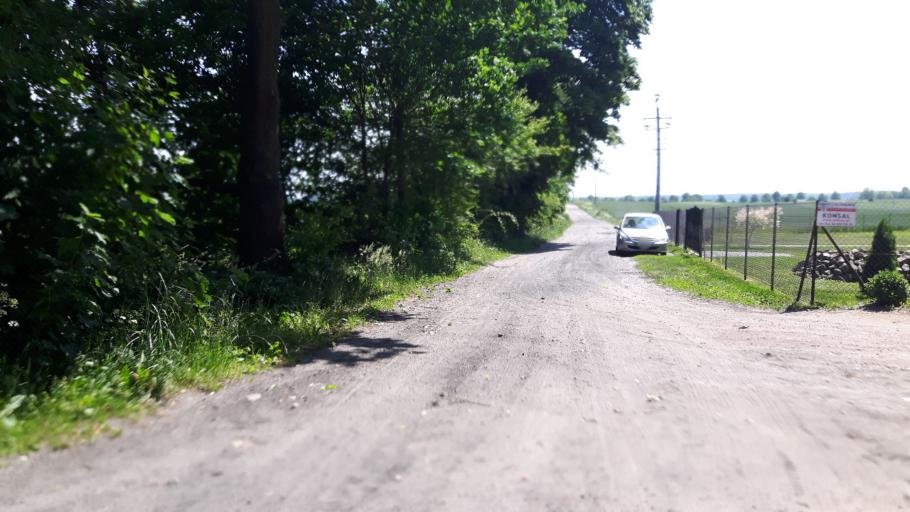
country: PL
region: Pomeranian Voivodeship
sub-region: Powiat wejherowski
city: Choczewo
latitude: 54.7309
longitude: 17.9546
